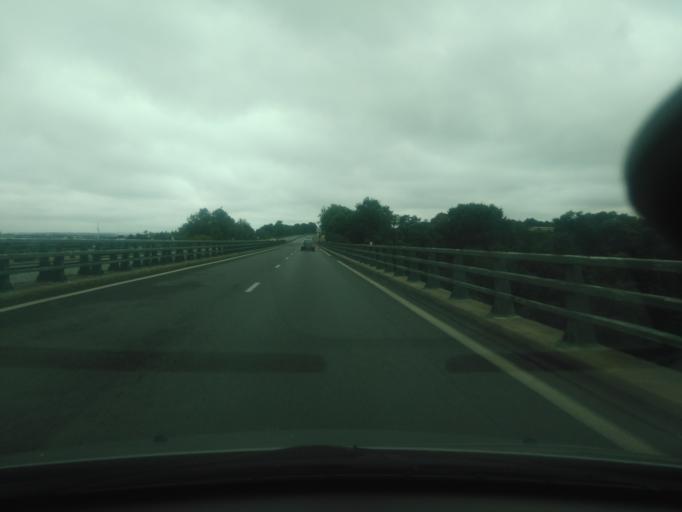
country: FR
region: Brittany
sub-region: Departement des Cotes-d'Armor
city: Jugon-les-Lacs
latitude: 48.4139
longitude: -2.3235
